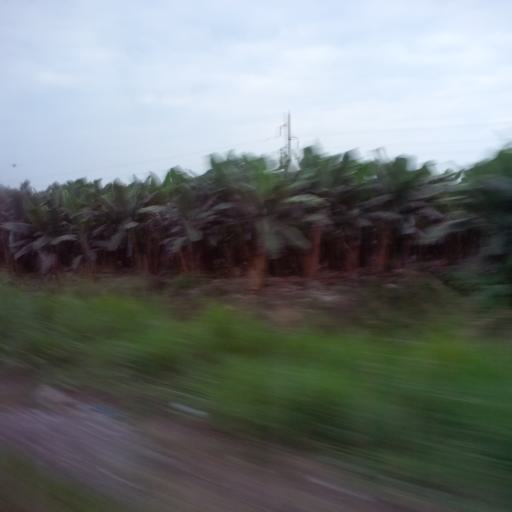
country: EC
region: Canar
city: La Troncal
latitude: -2.3455
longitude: -79.3670
